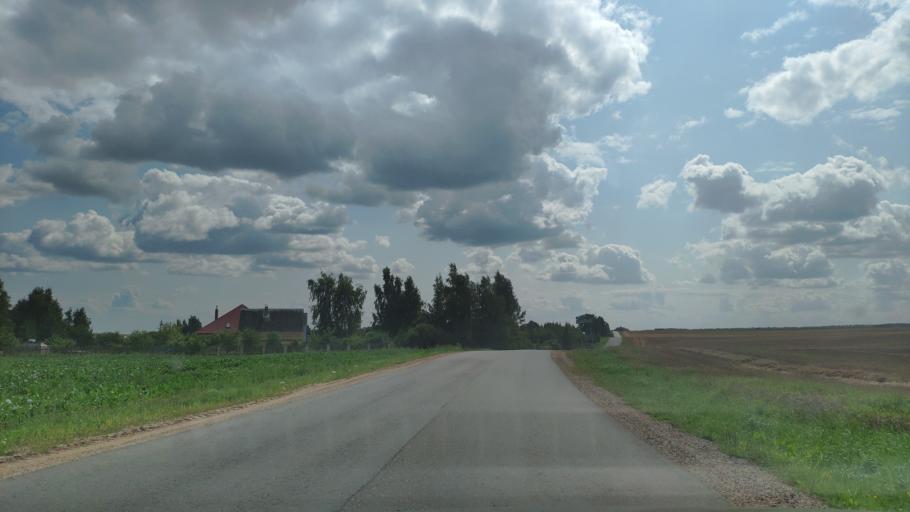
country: BY
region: Minsk
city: Khatsyezhyna
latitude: 53.8422
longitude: 27.3130
